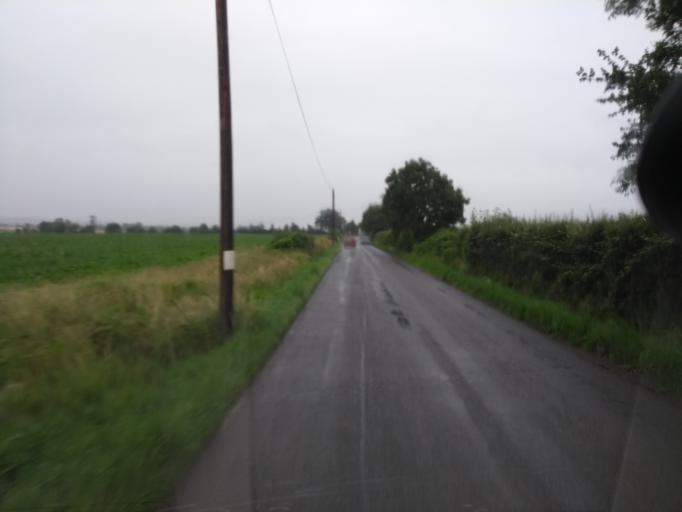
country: GB
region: England
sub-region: Somerset
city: Ilchester
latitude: 51.0732
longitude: -2.6849
